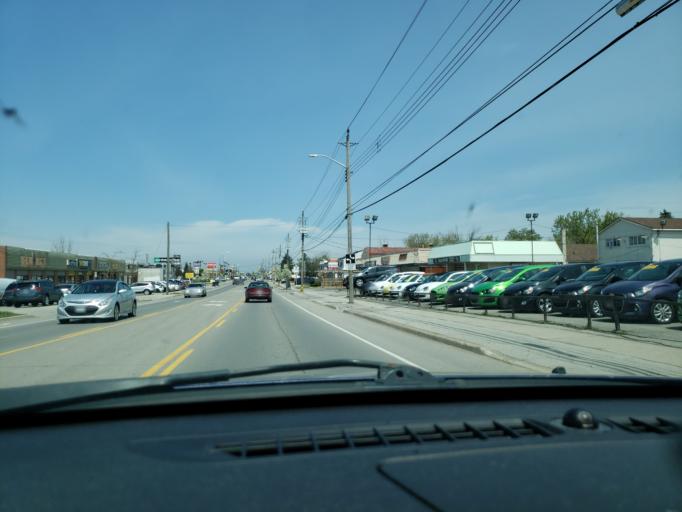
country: CA
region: Ontario
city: Thorold
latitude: 43.1445
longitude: -79.2141
